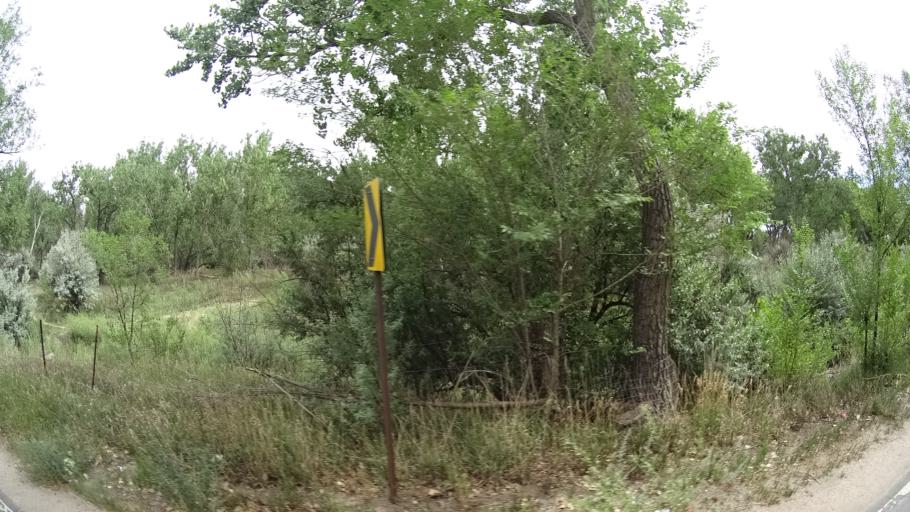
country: US
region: Colorado
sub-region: El Paso County
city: Fountain
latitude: 38.6752
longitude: -104.6980
